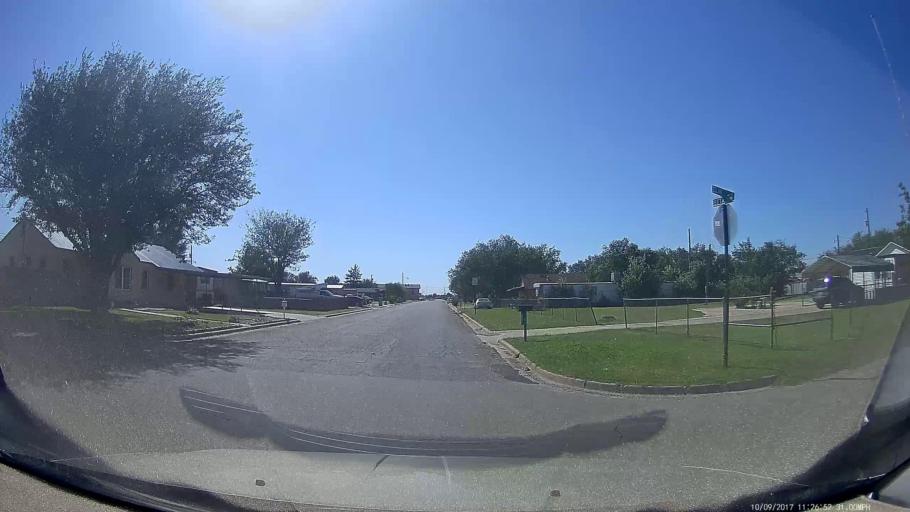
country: US
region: New Mexico
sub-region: Curry County
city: Clovis
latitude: 34.4079
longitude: -103.2272
